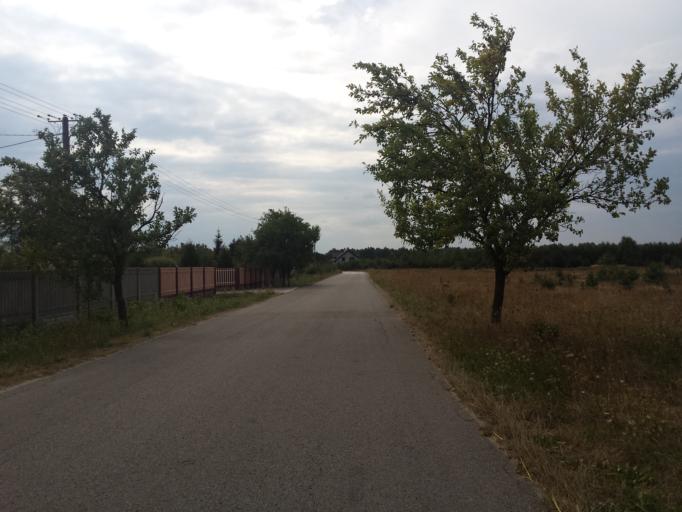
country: PL
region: Swietokrzyskie
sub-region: Powiat kielecki
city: Rakow
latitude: 50.6671
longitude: 21.1130
